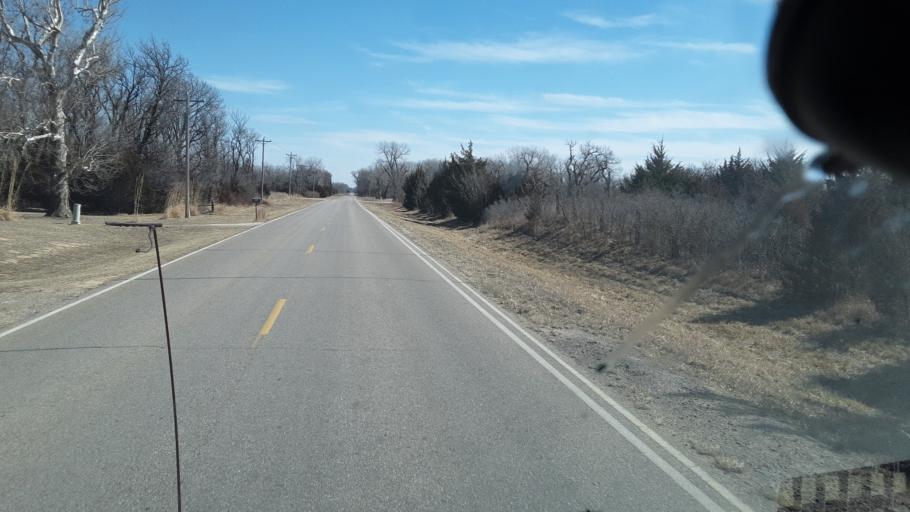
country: US
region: Kansas
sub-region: Reno County
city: Hutchinson
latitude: 38.1593
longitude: -97.9062
